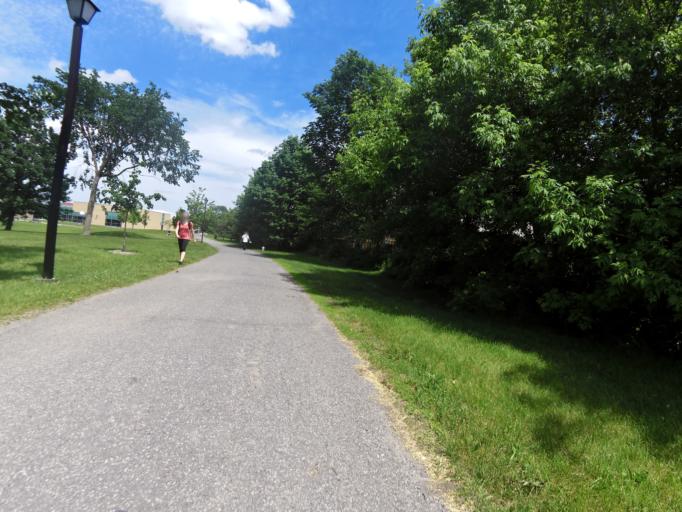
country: CA
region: Ontario
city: Ottawa
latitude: 45.3621
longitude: -75.6368
